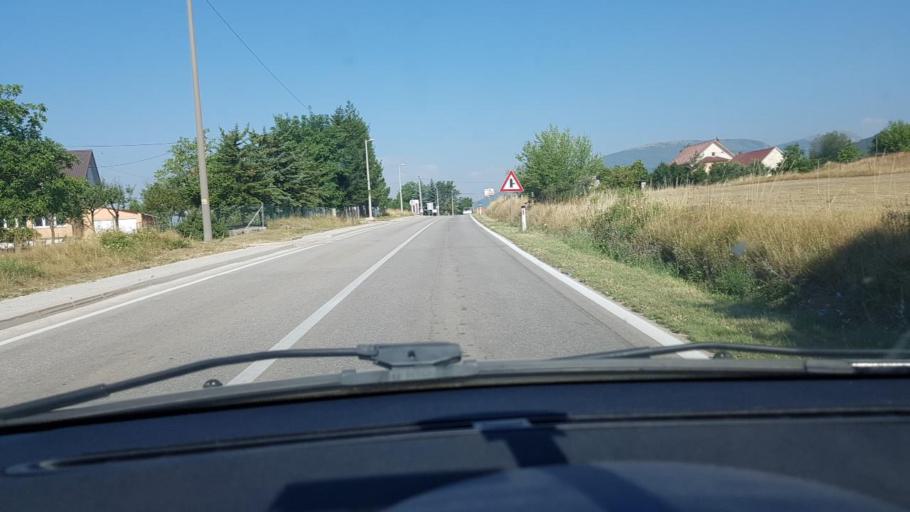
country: BA
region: Federation of Bosnia and Herzegovina
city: Livno
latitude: 43.8445
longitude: 16.9637
